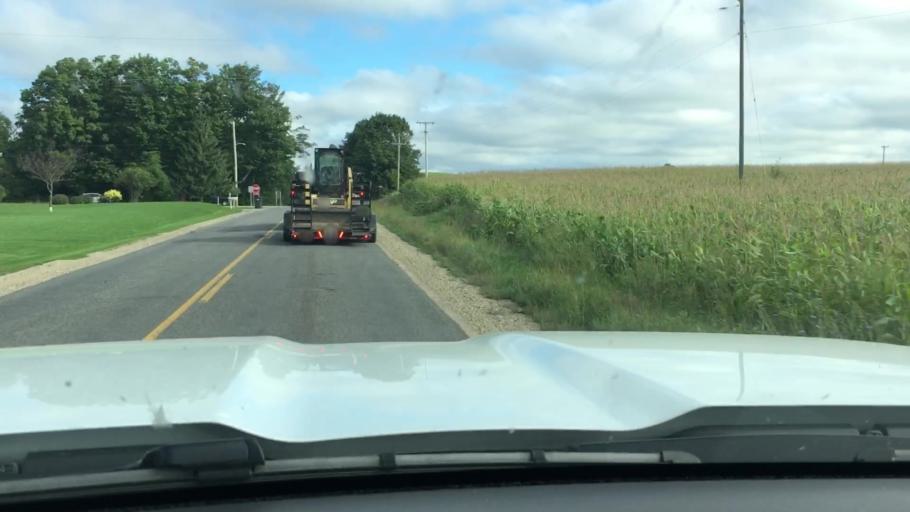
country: US
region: Michigan
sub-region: Kent County
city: Byron Center
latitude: 42.8104
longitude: -85.8026
